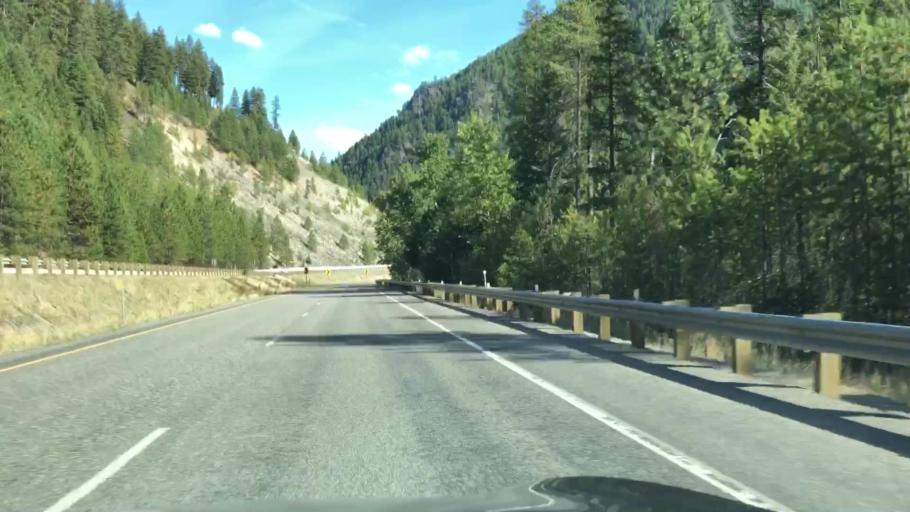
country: US
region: Montana
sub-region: Sanders County
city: Thompson Falls
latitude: 47.3154
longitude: -115.2395
